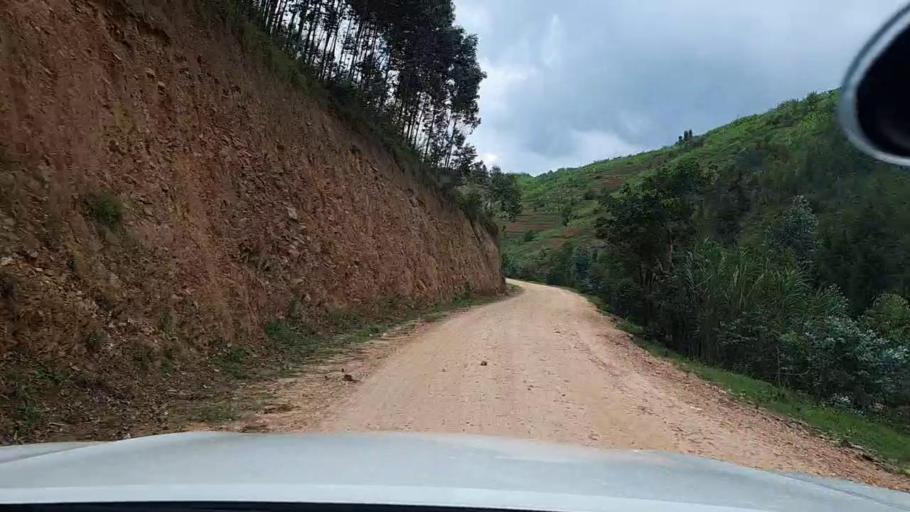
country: RW
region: Western Province
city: Kibuye
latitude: -2.1262
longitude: 29.4266
